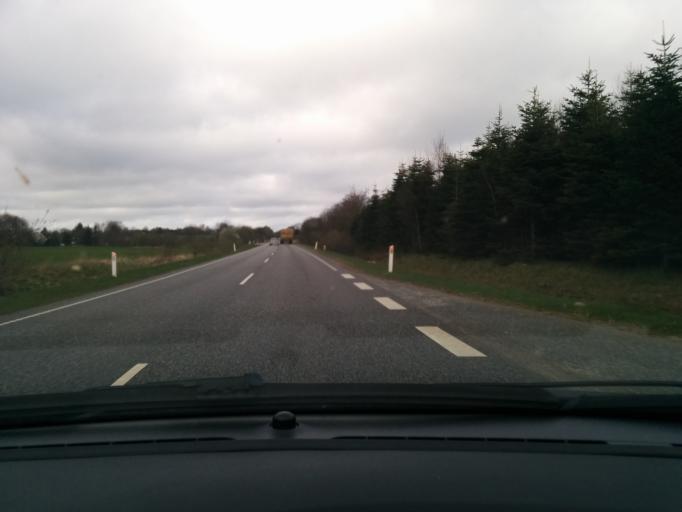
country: DK
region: Central Jutland
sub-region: Favrskov Kommune
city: Hammel
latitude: 56.2461
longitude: 9.8758
